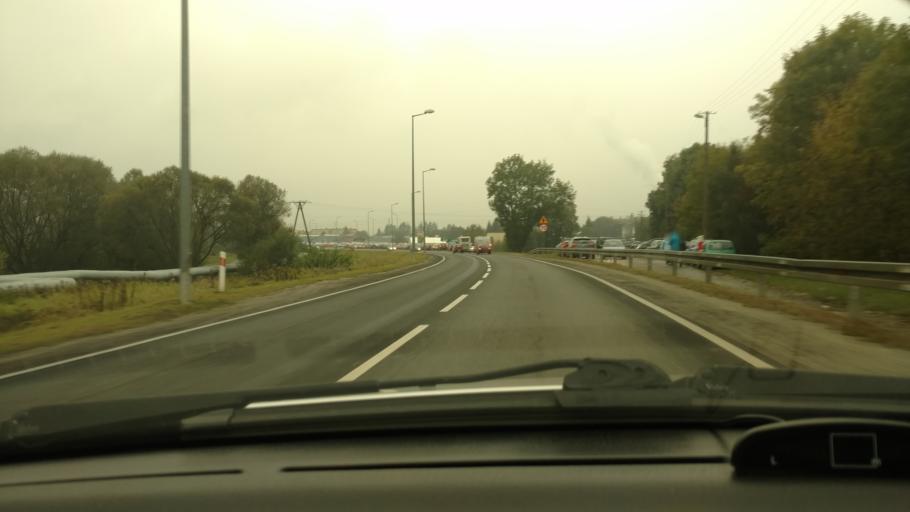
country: PL
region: Lesser Poland Voivodeship
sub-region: Powiat gorlicki
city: Gorlice
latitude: 49.6689
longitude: 21.1741
